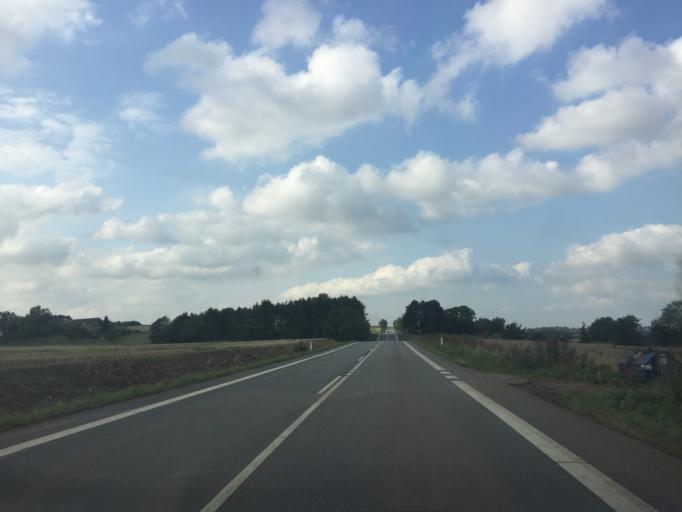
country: DK
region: Zealand
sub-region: Holbaek Kommune
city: Tollose
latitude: 55.6403
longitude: 11.7836
